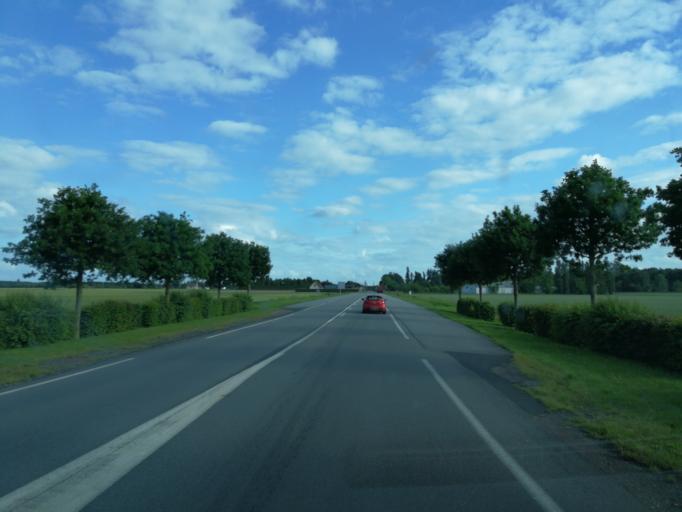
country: FR
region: Haute-Normandie
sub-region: Departement de l'Eure
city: Conches-en-Ouche
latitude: 48.9809
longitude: 0.9385
